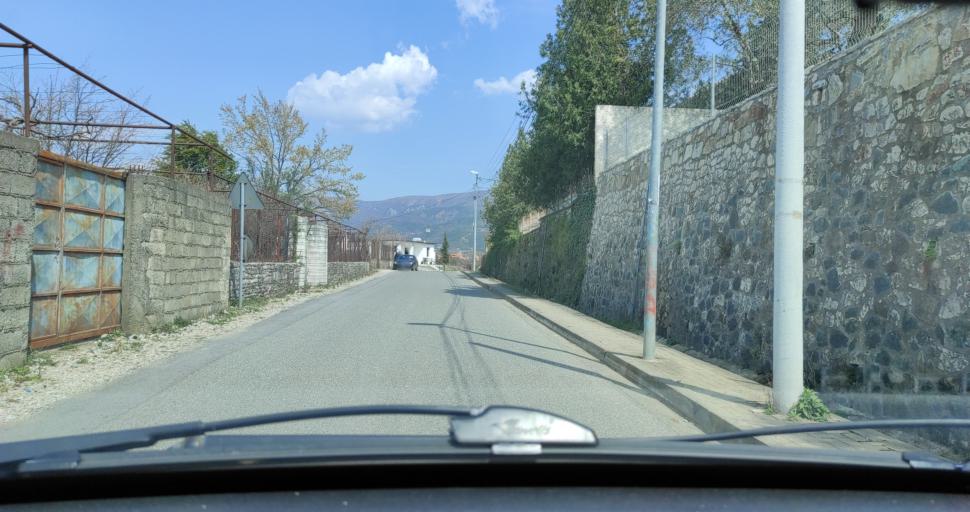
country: AL
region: Lezhe
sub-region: Rrethi i Lezhes
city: Kallmeti i Madh
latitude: 41.8502
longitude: 19.6914
